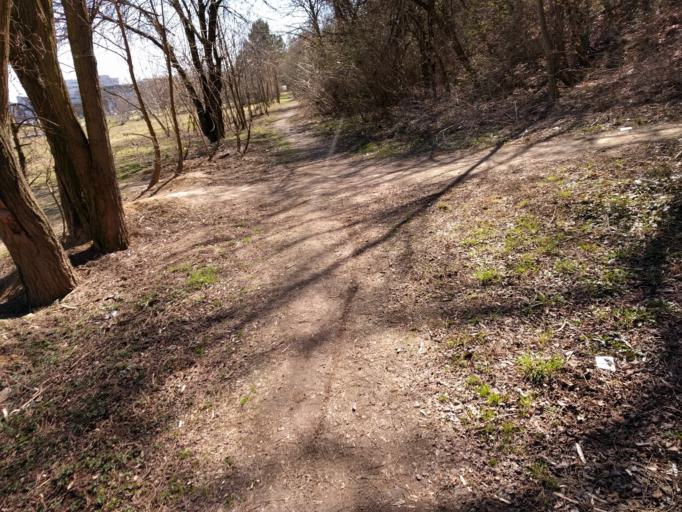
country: CZ
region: South Moravian
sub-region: Mesto Brno
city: Mokra Hora
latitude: 49.2309
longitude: 16.5745
